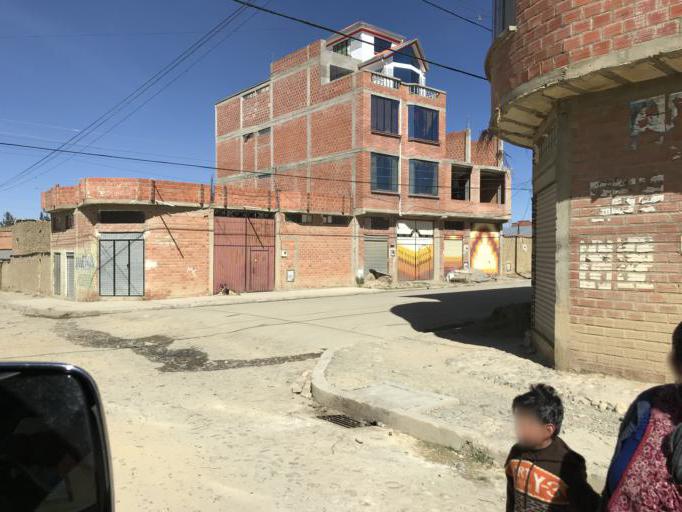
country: BO
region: La Paz
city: La Paz
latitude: -16.4861
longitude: -68.2106
